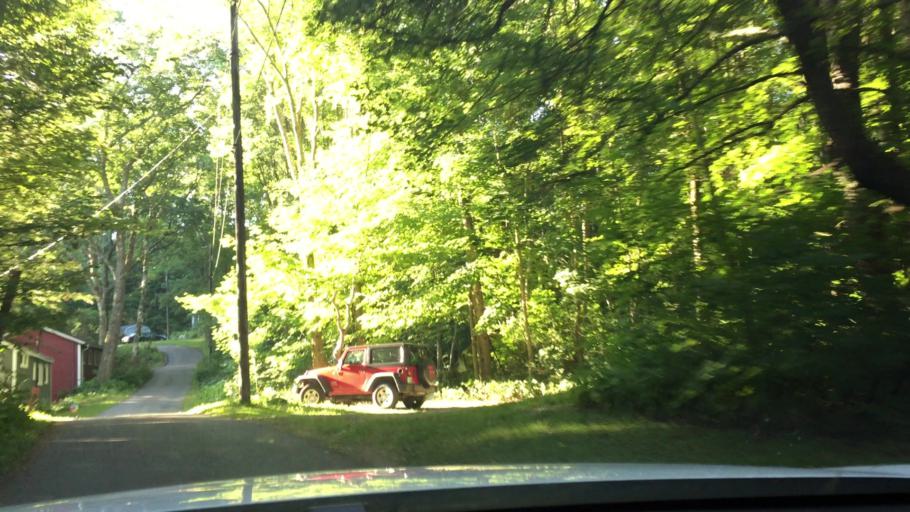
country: US
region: Massachusetts
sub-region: Berkshire County
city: Becket
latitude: 42.2810
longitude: -73.1452
